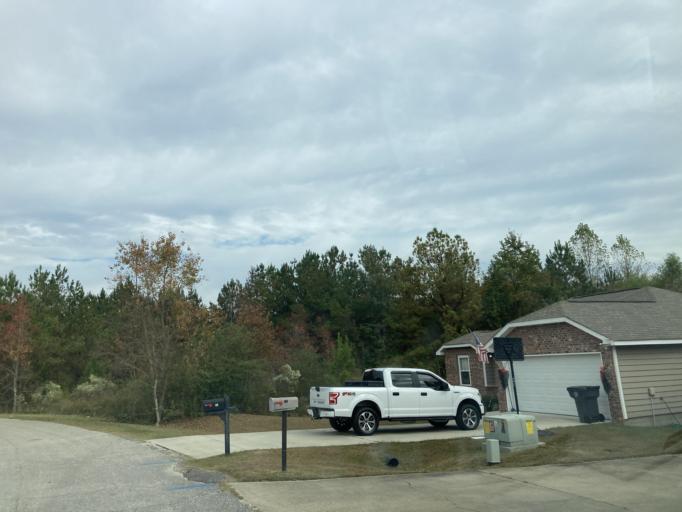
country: US
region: Mississippi
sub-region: Lamar County
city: West Hattiesburg
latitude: 31.2898
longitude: -89.3780
